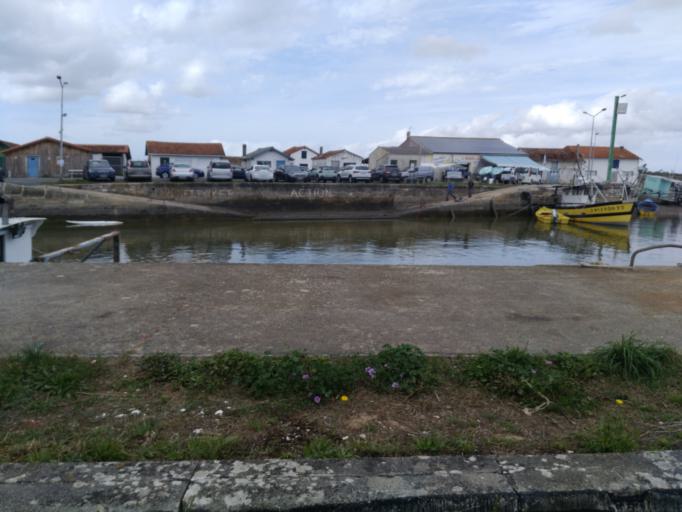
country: FR
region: Poitou-Charentes
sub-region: Departement de la Charente-Maritime
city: Le Gua
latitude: 45.7101
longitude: -0.9758
